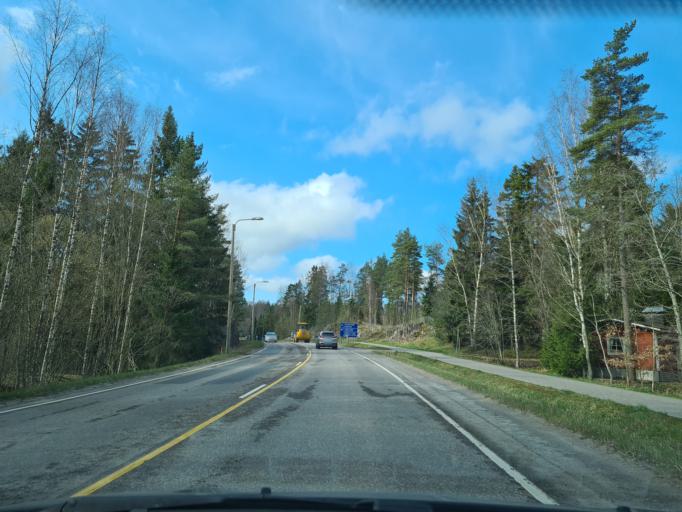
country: FI
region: Uusimaa
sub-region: Helsinki
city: Kirkkonummi
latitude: 60.0961
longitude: 24.4137
